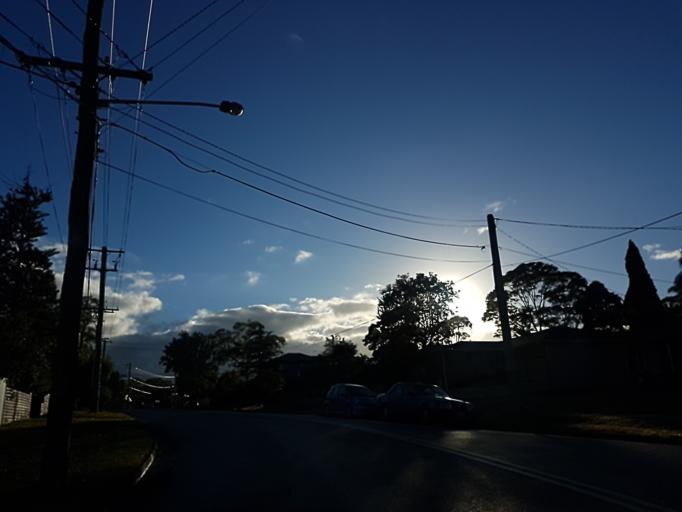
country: AU
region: New South Wales
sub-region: Warringah
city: Davidson
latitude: -33.7353
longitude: 151.2105
